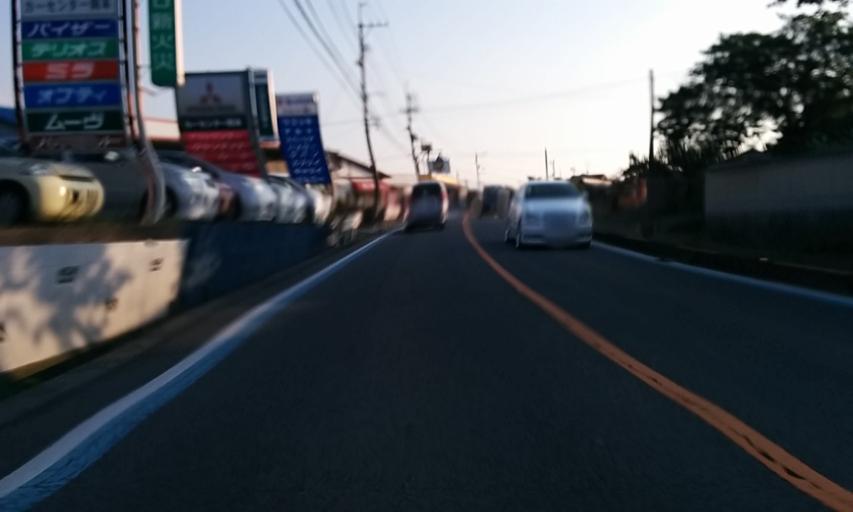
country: JP
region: Ehime
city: Masaki-cho
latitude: 33.7830
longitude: 132.7618
